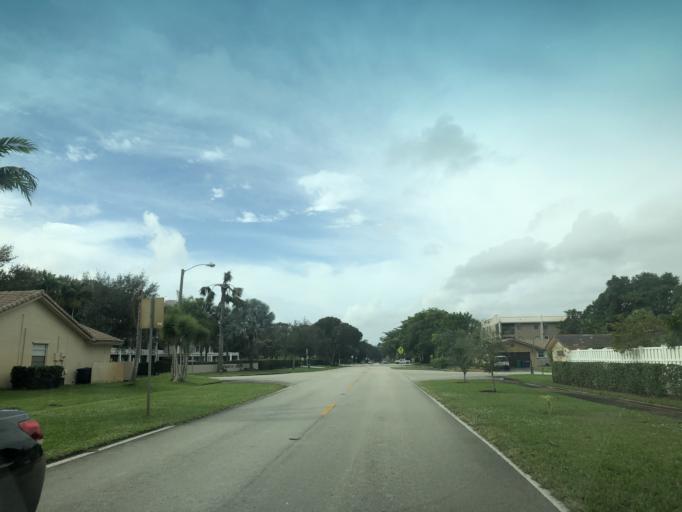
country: US
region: Florida
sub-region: Broward County
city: North Lauderdale
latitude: 26.2463
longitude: -80.2405
